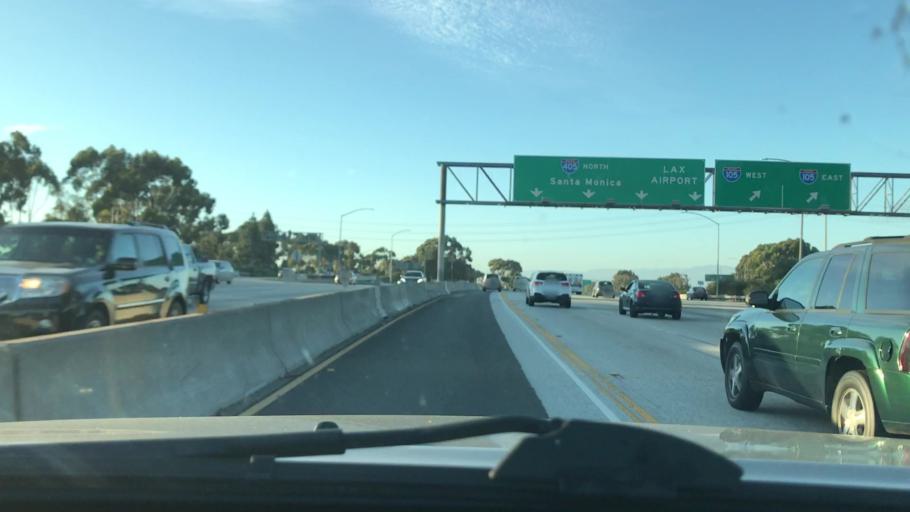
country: US
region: California
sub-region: Los Angeles County
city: Del Aire
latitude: 33.9138
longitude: -118.3698
